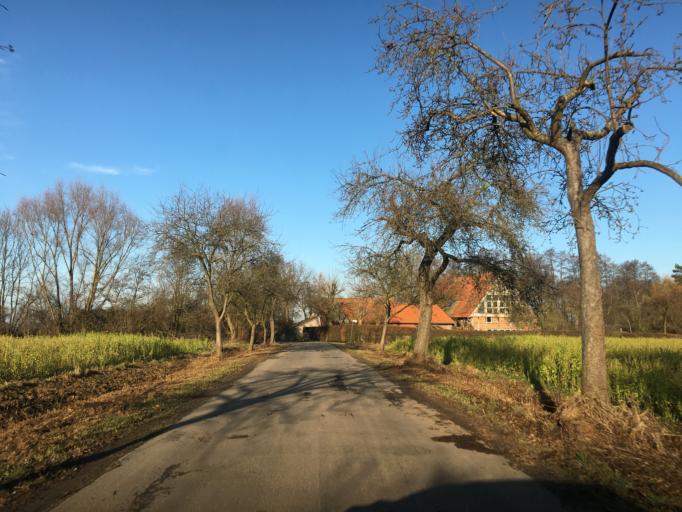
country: DE
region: North Rhine-Westphalia
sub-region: Regierungsbezirk Munster
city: Altenberge
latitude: 52.0389
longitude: 7.5222
